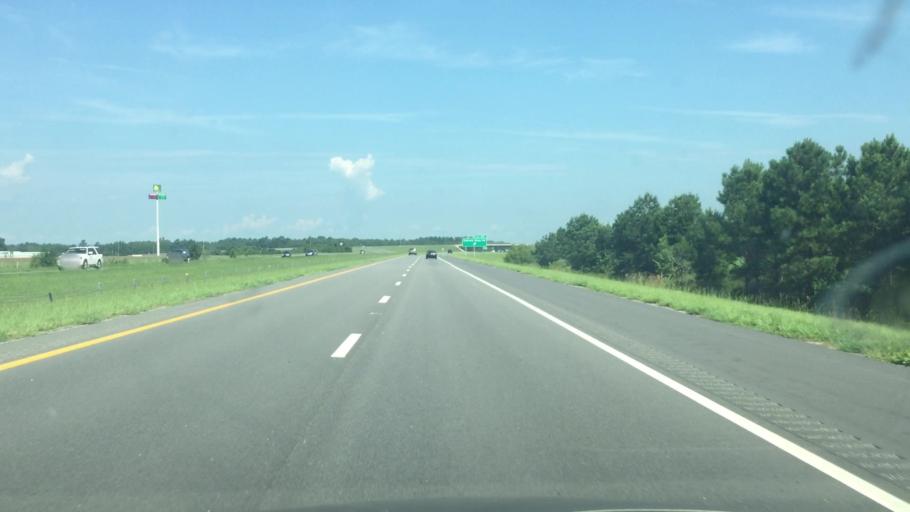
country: US
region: North Carolina
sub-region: Robeson County
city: Pembroke
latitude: 34.6753
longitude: -79.2695
